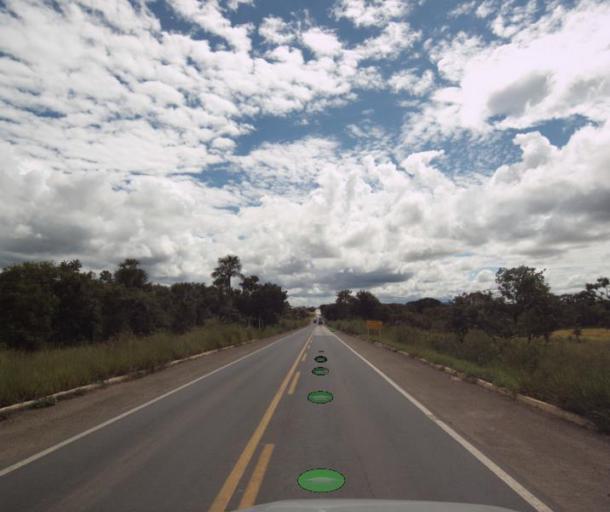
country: BR
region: Goias
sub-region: Uruacu
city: Uruacu
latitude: -14.3242
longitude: -49.1522
